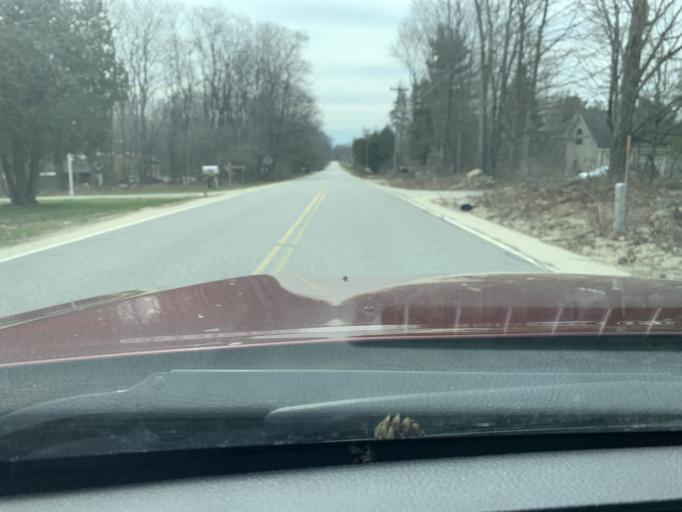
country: US
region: Maine
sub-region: Androscoggin County
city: Poland
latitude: 43.9627
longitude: -70.3914
